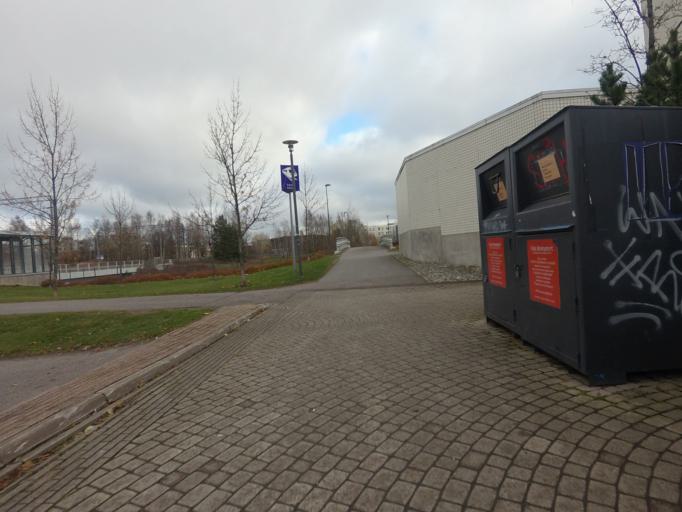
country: FI
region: Uusimaa
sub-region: Helsinki
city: Espoo
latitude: 60.2054
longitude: 24.6607
